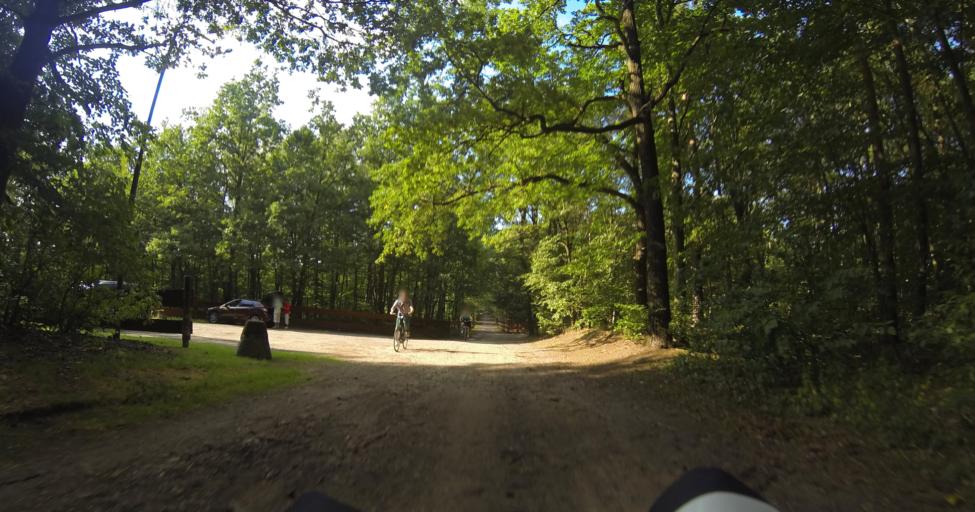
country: DE
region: Saxony
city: Moritzburg
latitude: 51.1501
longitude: 13.6910
